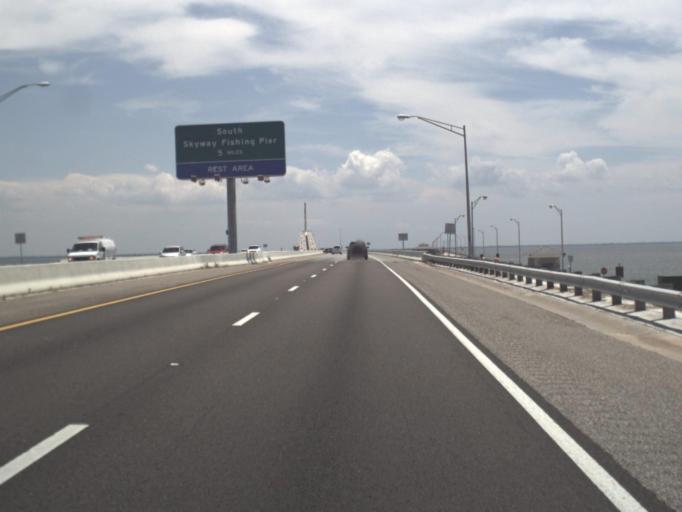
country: US
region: Florida
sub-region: Pinellas County
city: Tierra Verde
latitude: 27.6412
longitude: -82.6706
